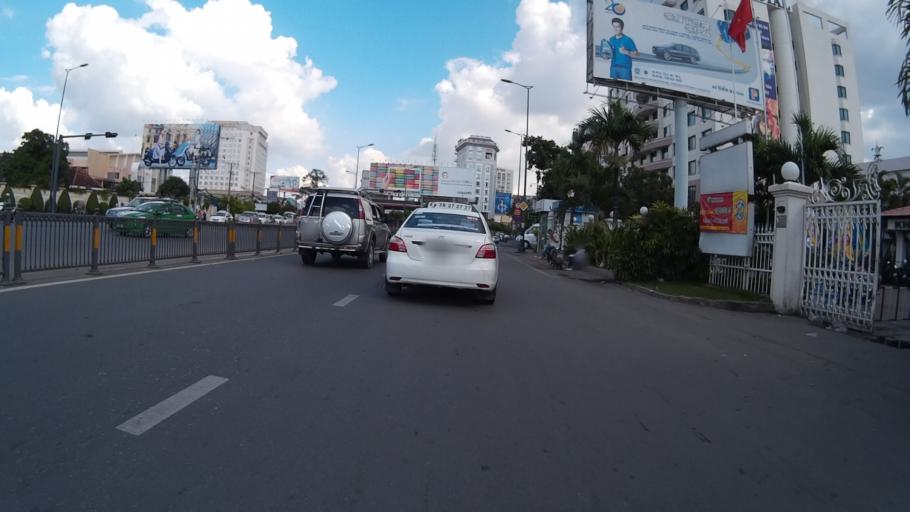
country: VN
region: Ho Chi Minh City
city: Quan Phu Nhuan
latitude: 10.8001
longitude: 106.6674
